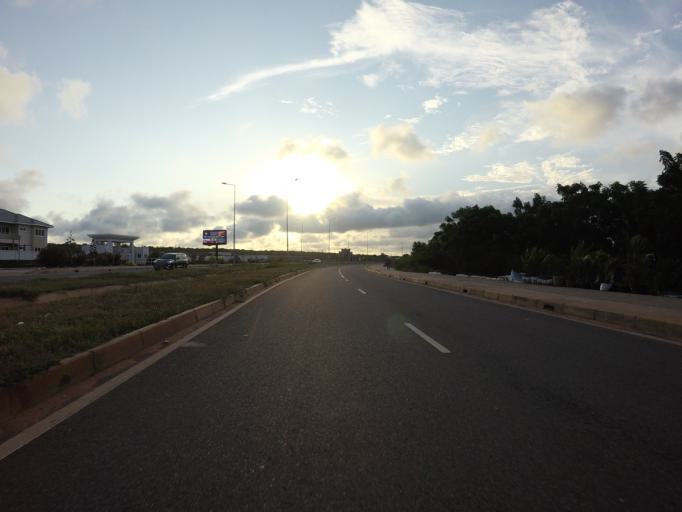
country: GH
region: Greater Accra
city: Teshi Old Town
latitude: 5.6102
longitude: -0.1442
